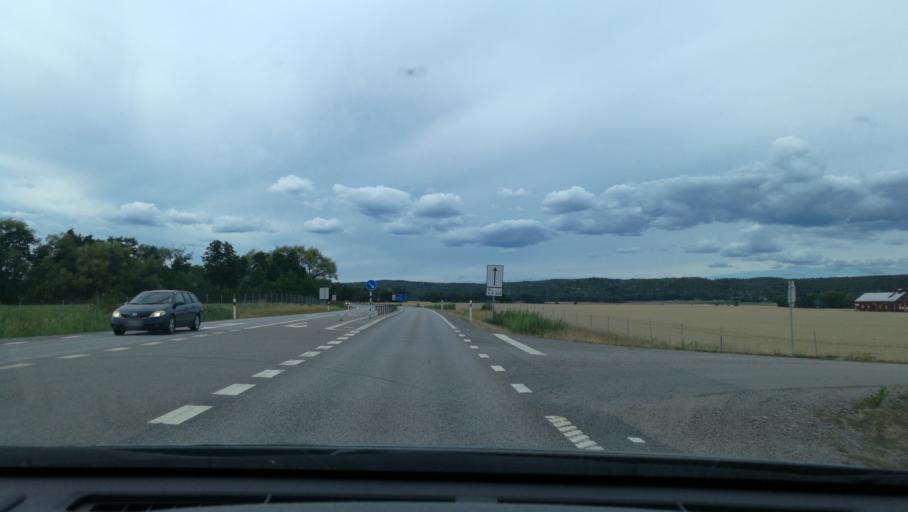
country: SE
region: OEstergoetland
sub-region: Norrkopings Kommun
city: Norrkoping
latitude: 58.6304
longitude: 16.1438
